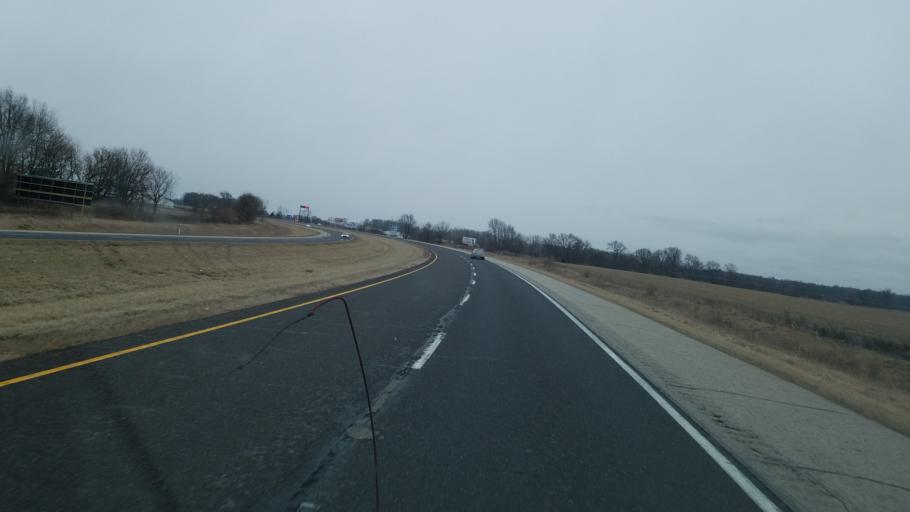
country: US
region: Indiana
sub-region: Fulton County
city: Rochester
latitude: 41.0519
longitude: -86.2381
